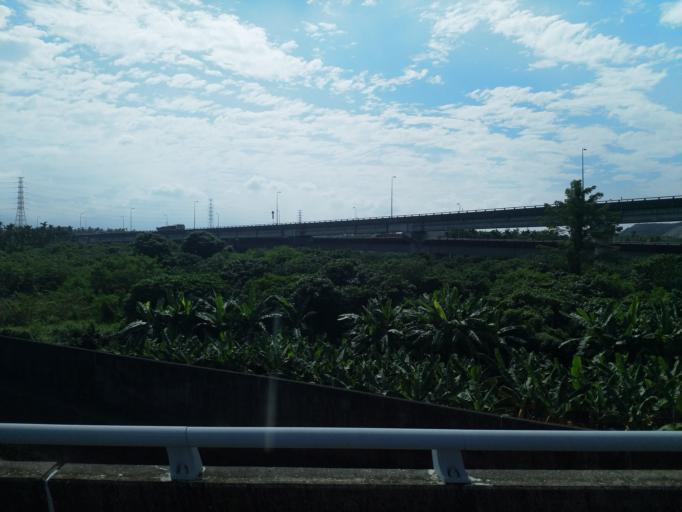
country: TW
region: Taiwan
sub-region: Pingtung
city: Pingtung
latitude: 22.8010
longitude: 120.4762
